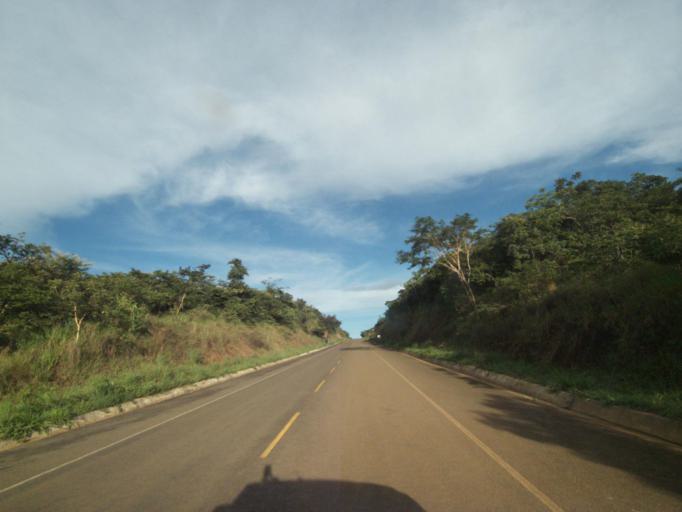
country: BR
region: Goias
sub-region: Jaragua
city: Jaragua
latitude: -15.8424
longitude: -49.3441
